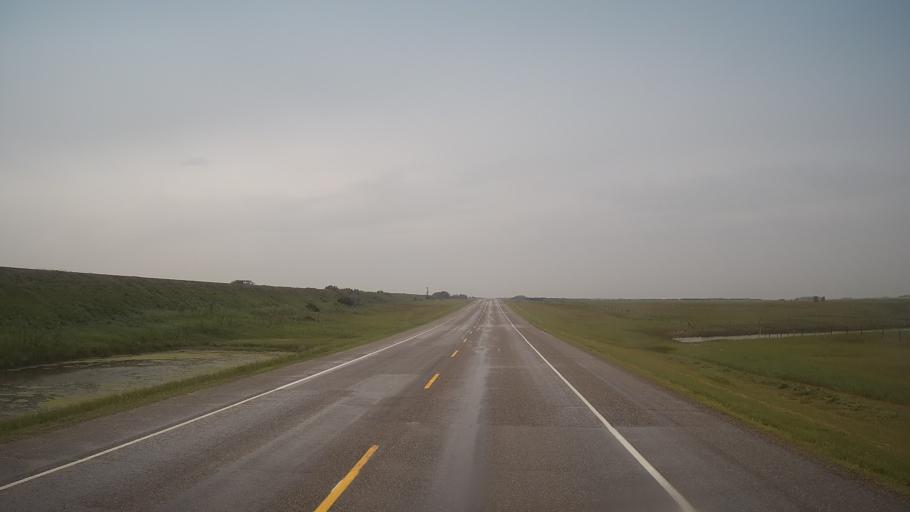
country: CA
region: Saskatchewan
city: Wilkie
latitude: 52.2152
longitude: -108.5020
